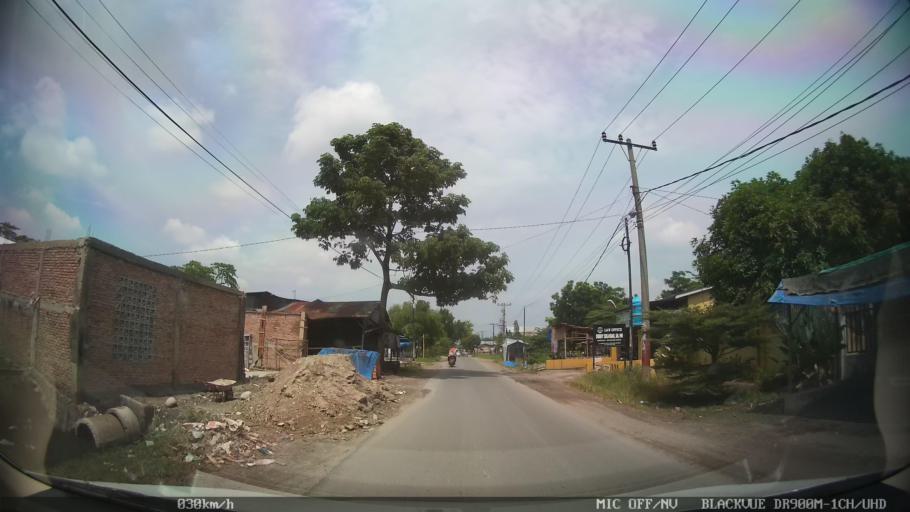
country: ID
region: North Sumatra
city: Medan
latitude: 3.6508
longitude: 98.7069
